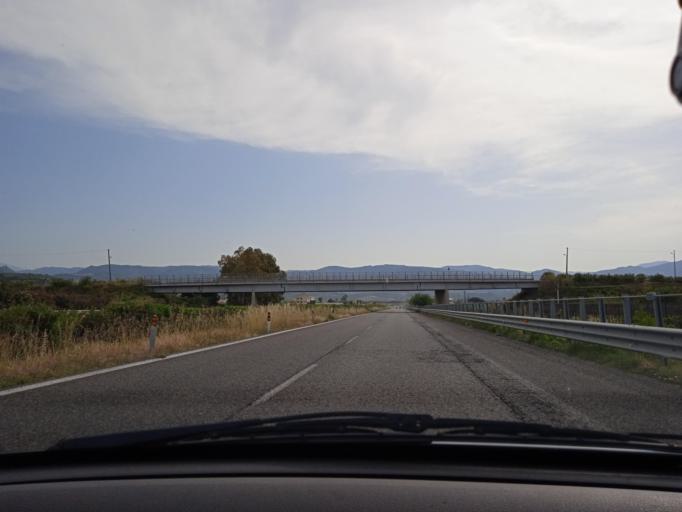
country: IT
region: Sicily
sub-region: Messina
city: Vigliatore 2
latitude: 38.1301
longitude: 15.1315
